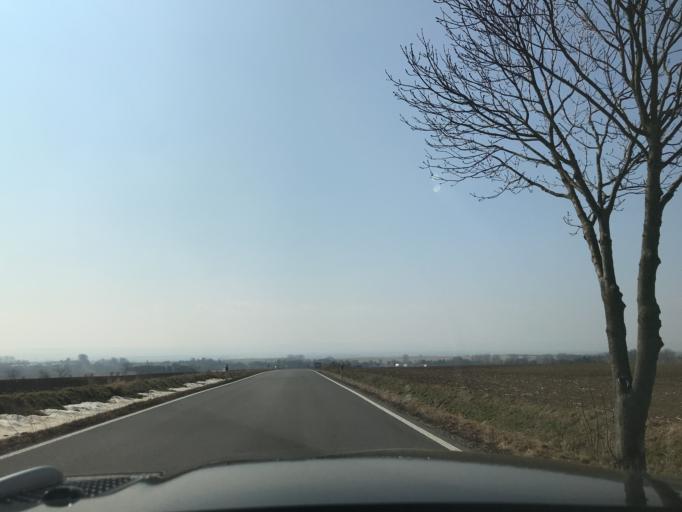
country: DE
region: Thuringia
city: Issersheilingen
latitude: 51.1970
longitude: 10.6369
